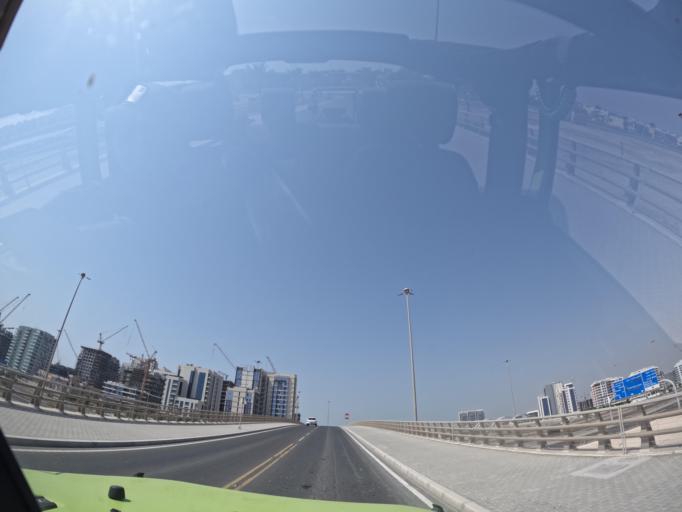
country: AE
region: Abu Dhabi
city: Abu Dhabi
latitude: 24.4420
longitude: 54.5927
